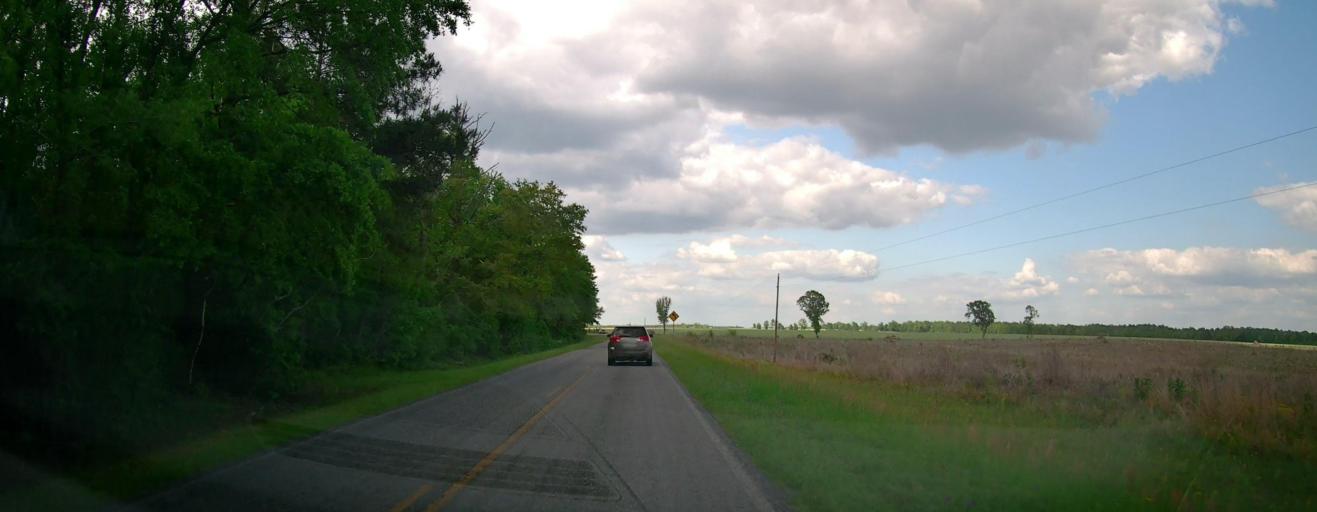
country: US
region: Georgia
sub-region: Laurens County
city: East Dublin
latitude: 32.6790
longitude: -82.8932
